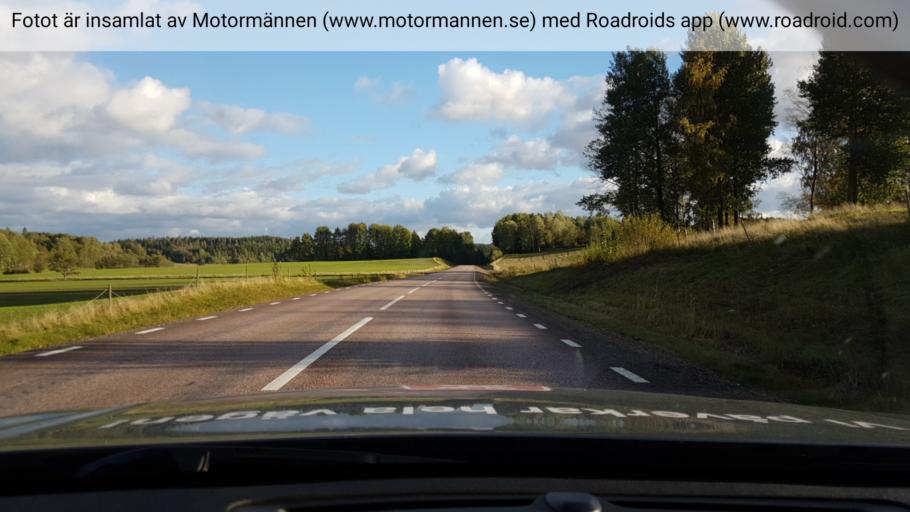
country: SE
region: Vaermland
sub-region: Karlstads Kommun
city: Molkom
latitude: 59.6303
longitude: 13.7270
